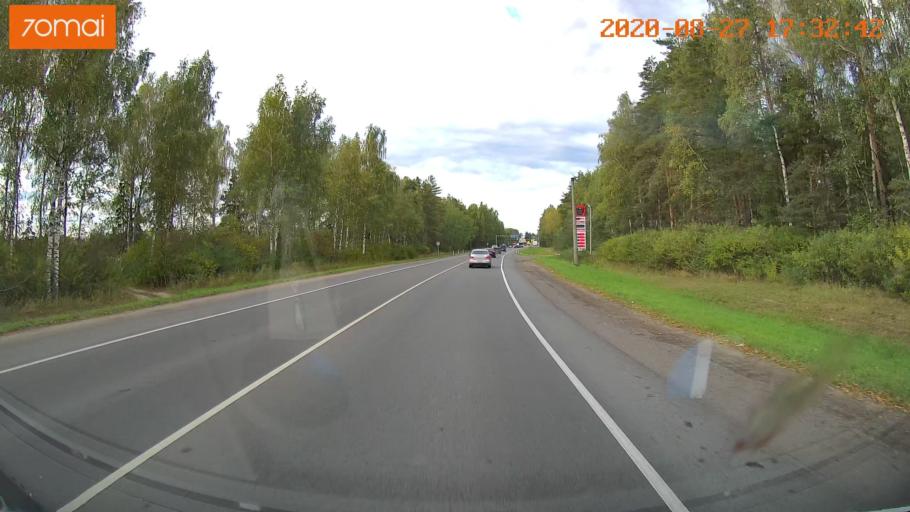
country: RU
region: Ivanovo
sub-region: Gorod Ivanovo
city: Ivanovo
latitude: 56.9305
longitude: 40.9642
